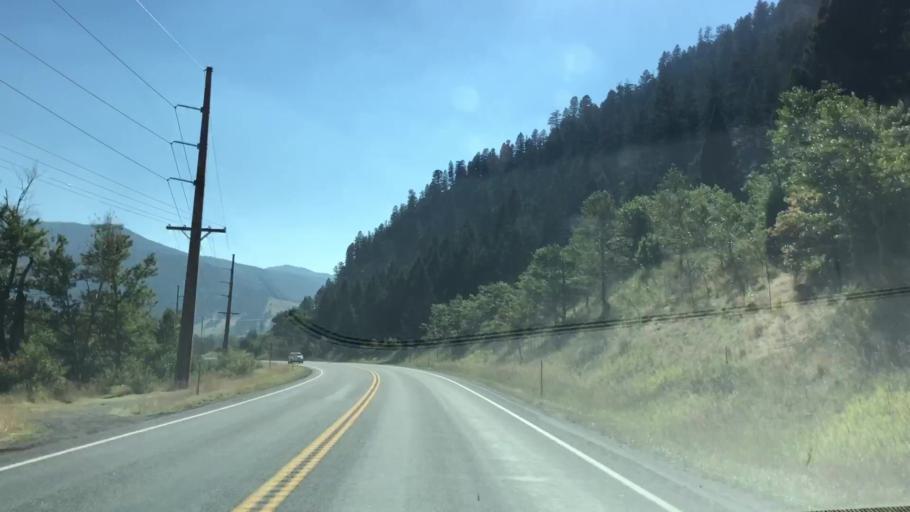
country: US
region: Montana
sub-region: Gallatin County
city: Four Corners
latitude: 45.5056
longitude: -111.2659
